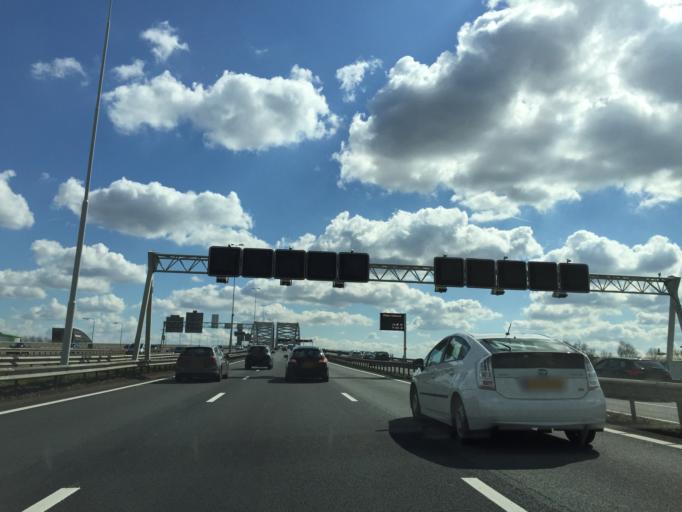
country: NL
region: South Holland
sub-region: Gemeente Rotterdam
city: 's-Gravenland
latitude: 51.9102
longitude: 4.5384
